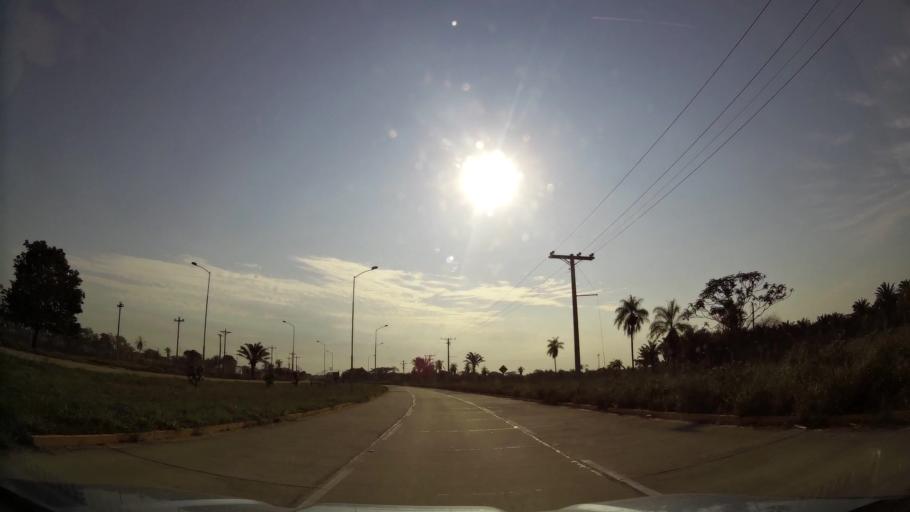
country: BO
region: Santa Cruz
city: Santa Cruz de la Sierra
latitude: -17.6915
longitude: -63.1158
